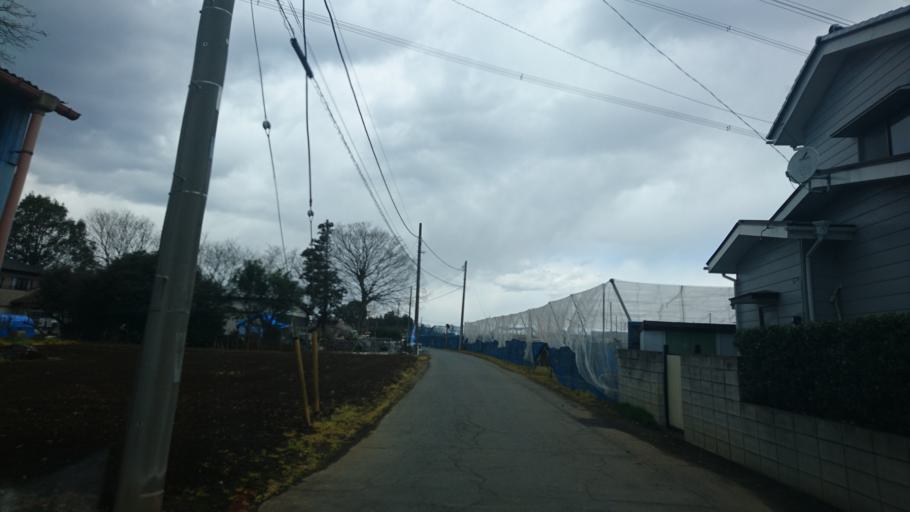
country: JP
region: Ibaraki
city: Yuki
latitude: 36.2672
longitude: 139.9130
